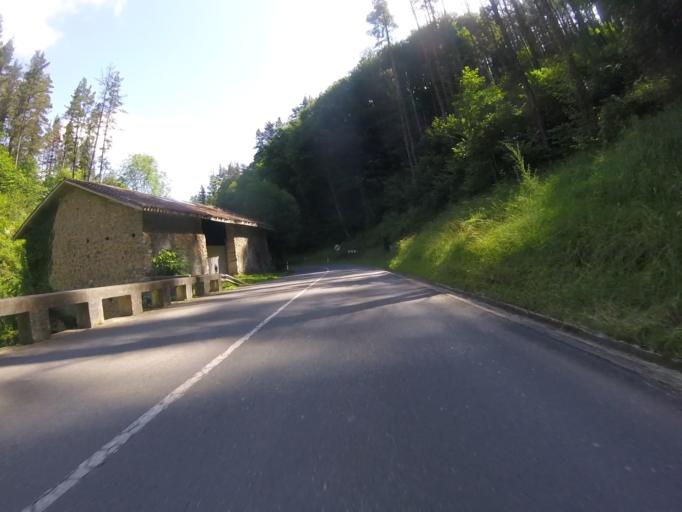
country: ES
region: Basque Country
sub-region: Provincia de Guipuzcoa
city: Beizama
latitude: 43.1011
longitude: -2.2428
